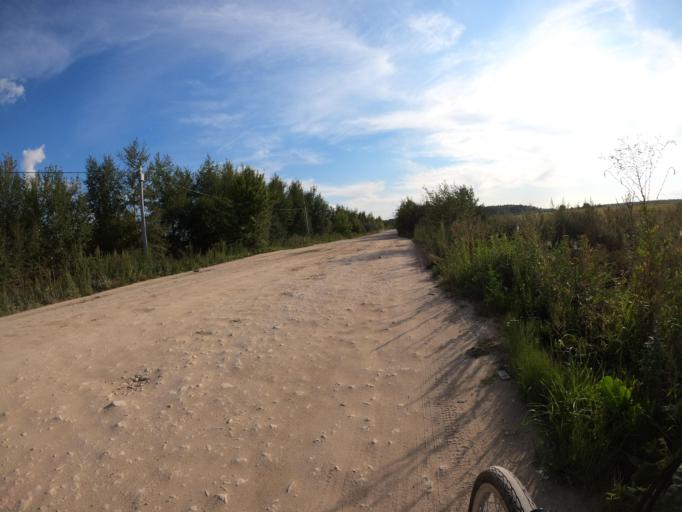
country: RU
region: Moskovskaya
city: Meshcherino
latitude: 55.1426
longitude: 38.4376
